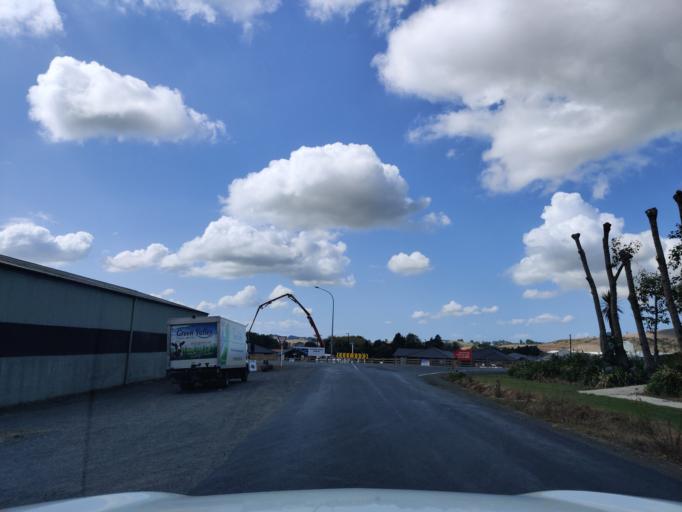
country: NZ
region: Auckland
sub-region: Auckland
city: Pukekohe East
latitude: -37.2429
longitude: 175.0161
